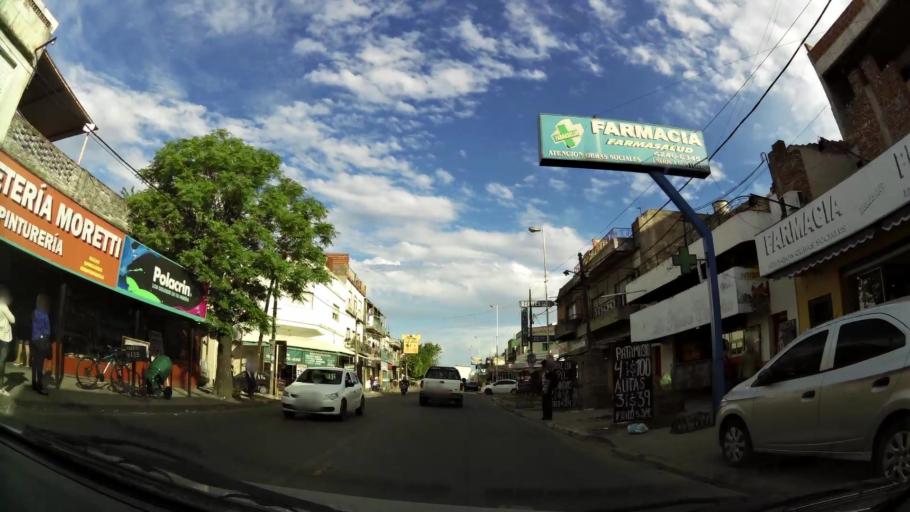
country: AR
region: Buenos Aires
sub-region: Partido de Lanus
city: Lanus
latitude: -34.7097
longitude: -58.3535
